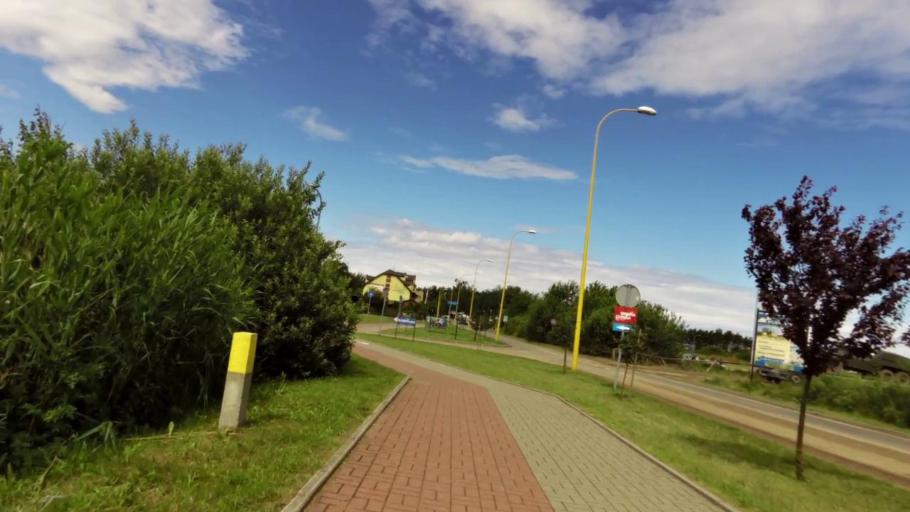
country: PL
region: West Pomeranian Voivodeship
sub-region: Powiat slawienski
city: Darlowo
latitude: 54.4439
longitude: 16.3985
